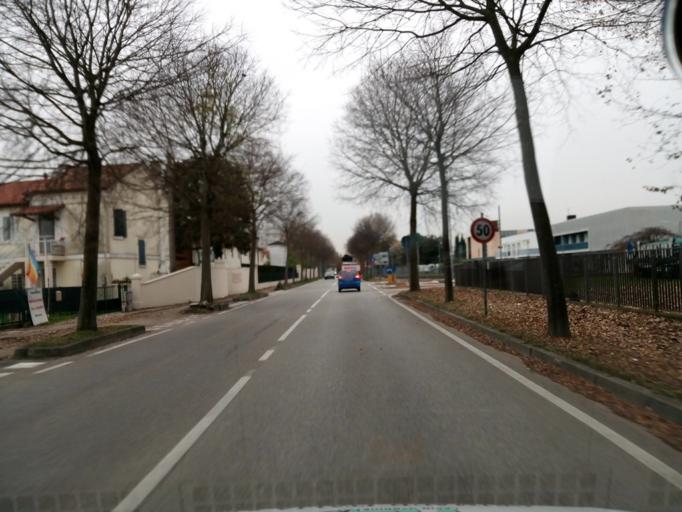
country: IT
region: Veneto
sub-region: Provincia di Padova
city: Vigonza
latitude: 45.4349
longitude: 11.9593
